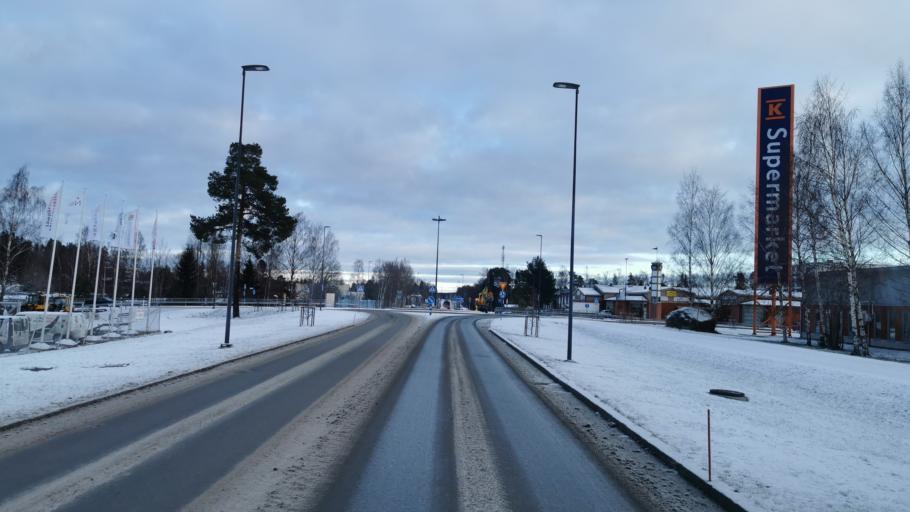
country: FI
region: Ostrobothnia
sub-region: Vaasa
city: Korsholm
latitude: 63.1124
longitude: 21.6754
